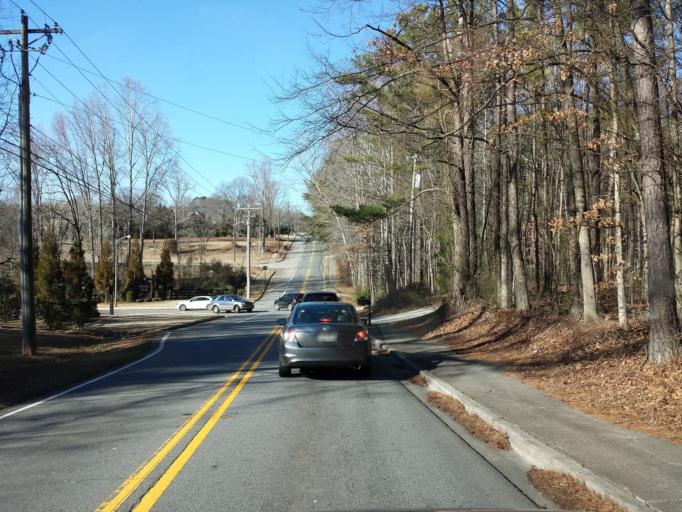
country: US
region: Georgia
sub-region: Cobb County
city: Kennesaw
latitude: 33.9579
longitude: -84.6615
